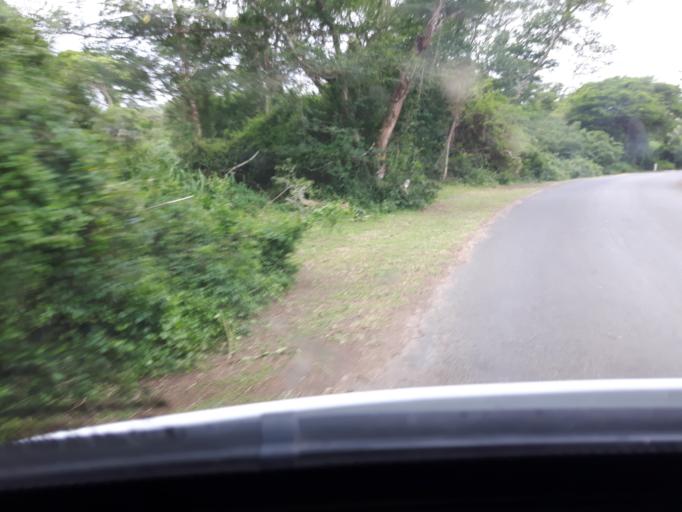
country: ZA
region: KwaZulu-Natal
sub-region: uMkhanyakude District Municipality
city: Mtubatuba
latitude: -28.3836
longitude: 32.4160
